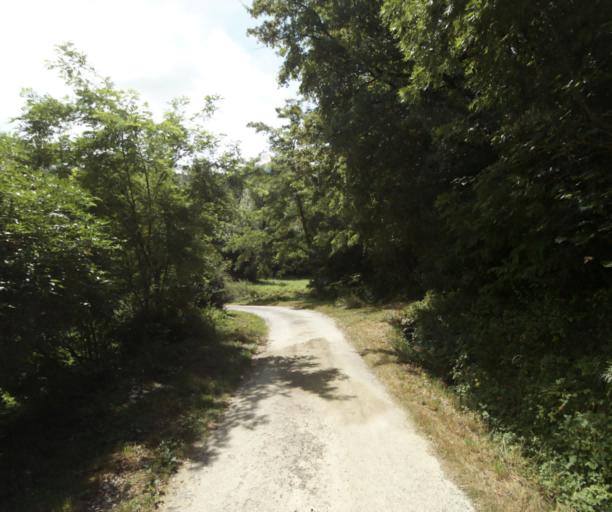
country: FR
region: Midi-Pyrenees
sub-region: Departement du Tarn
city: Dourgne
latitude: 43.4679
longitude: 2.1156
